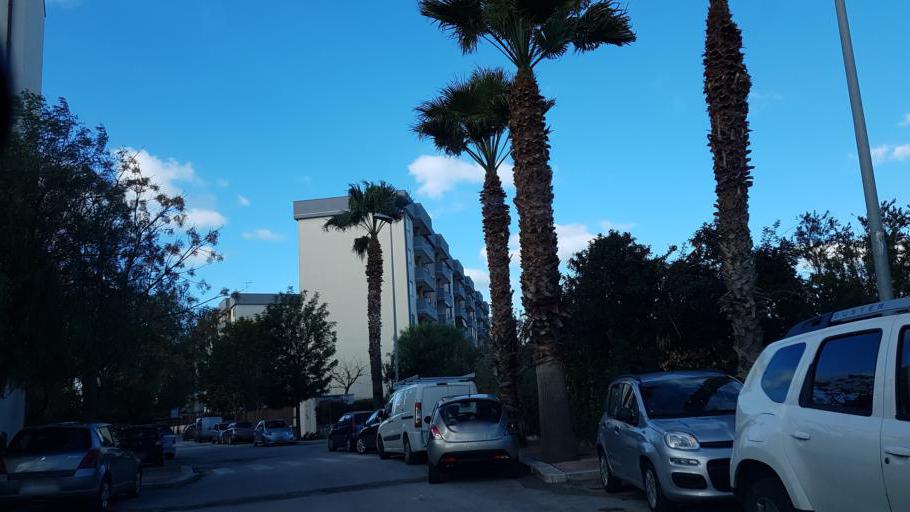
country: IT
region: Apulia
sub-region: Provincia di Brindisi
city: Brindisi
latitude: 40.6496
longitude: 17.9228
